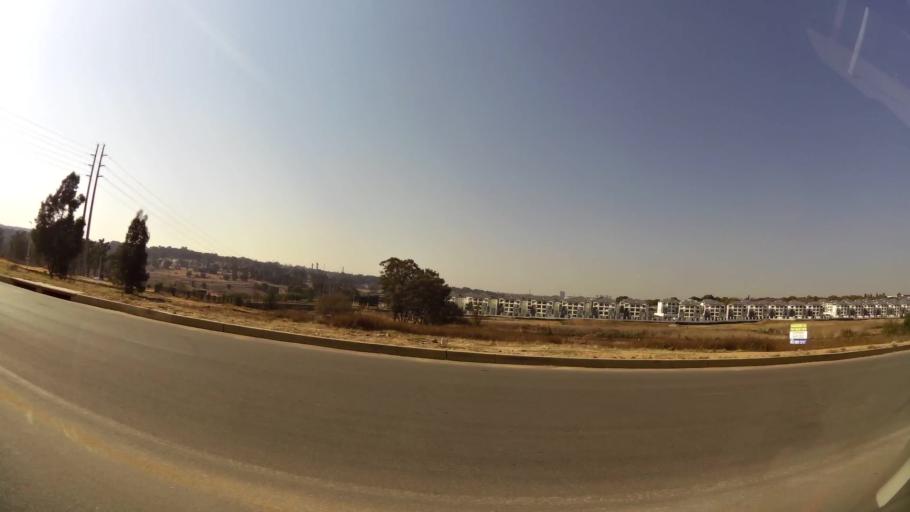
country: ZA
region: Gauteng
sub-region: City of Johannesburg Metropolitan Municipality
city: Modderfontein
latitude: -26.0949
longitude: 28.1420
